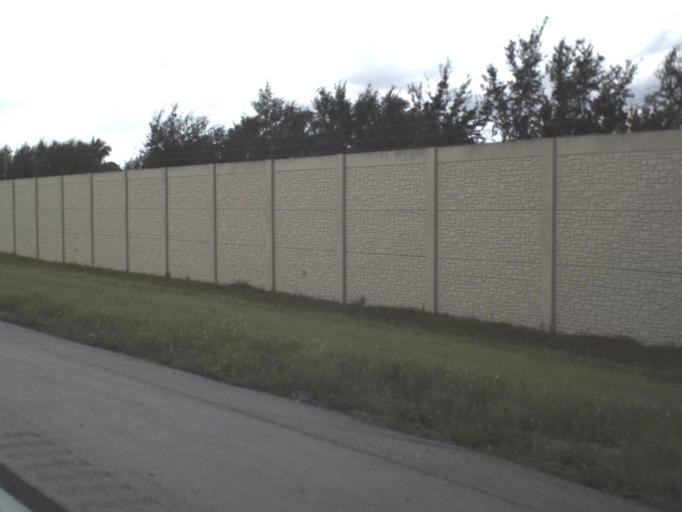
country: US
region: Florida
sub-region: Collier County
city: Vineyards
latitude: 26.2408
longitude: -81.7369
